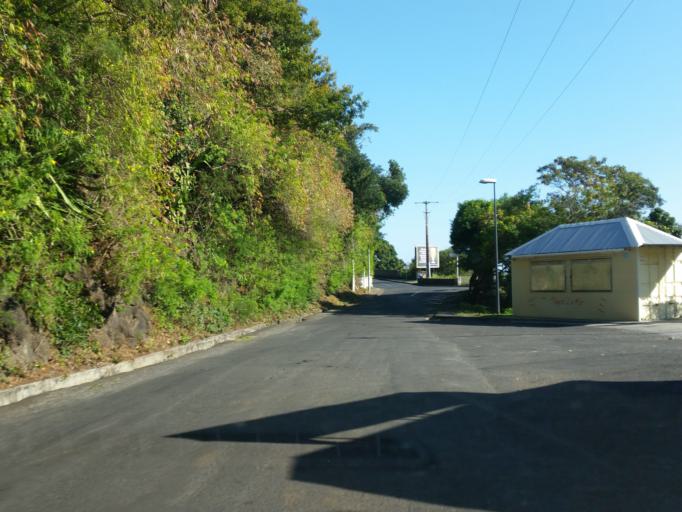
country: RE
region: Reunion
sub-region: Reunion
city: Sainte-Marie
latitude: -20.9172
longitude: 55.5096
